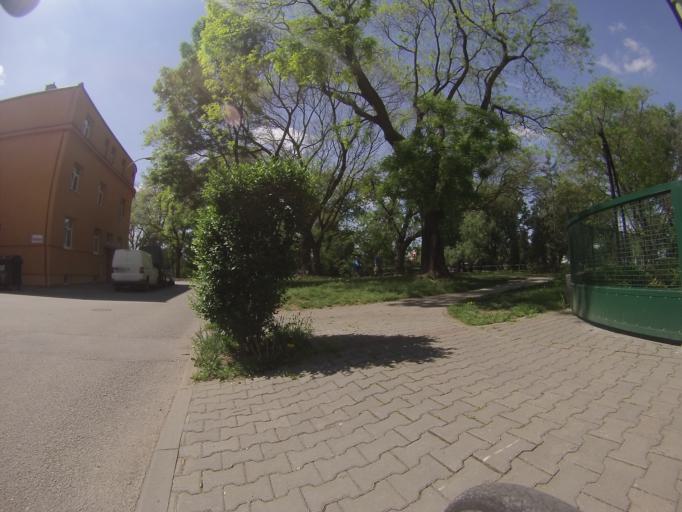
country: CZ
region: South Moravian
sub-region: Mesto Brno
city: Brno
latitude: 49.1769
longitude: 16.6182
